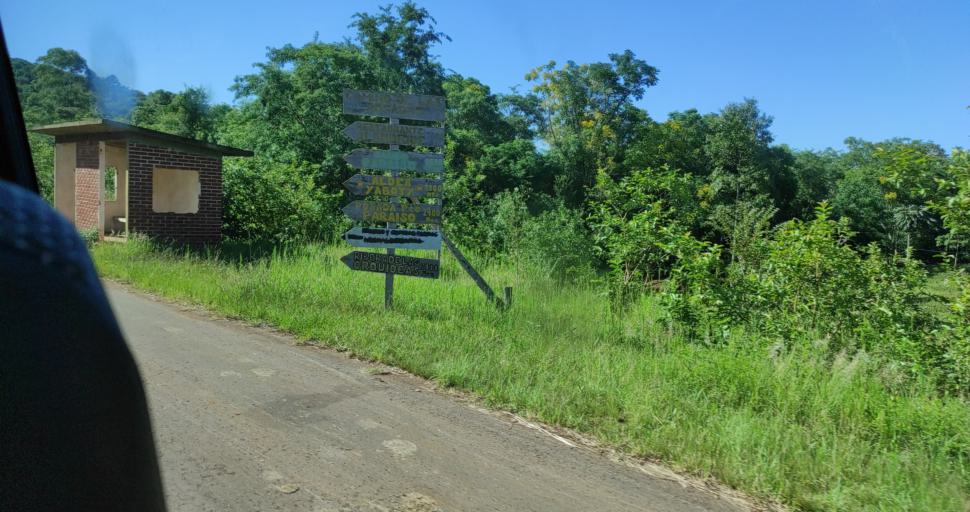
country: AR
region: Misiones
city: El Soberbio
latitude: -27.2414
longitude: -54.0406
